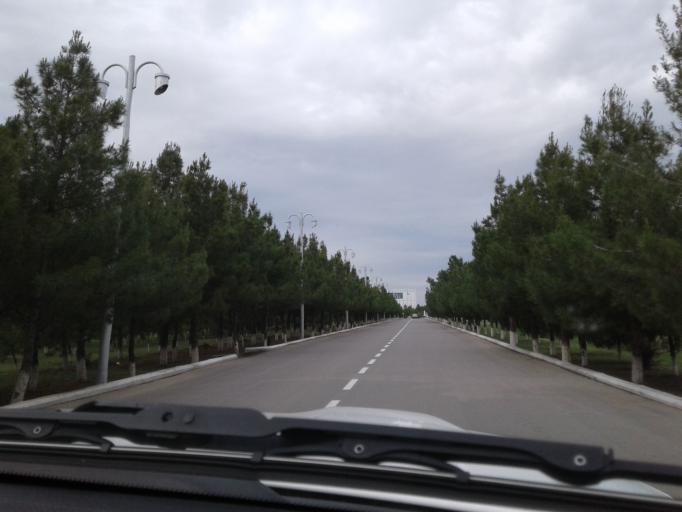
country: TM
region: Mary
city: Mary
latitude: 37.6038
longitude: 61.9024
